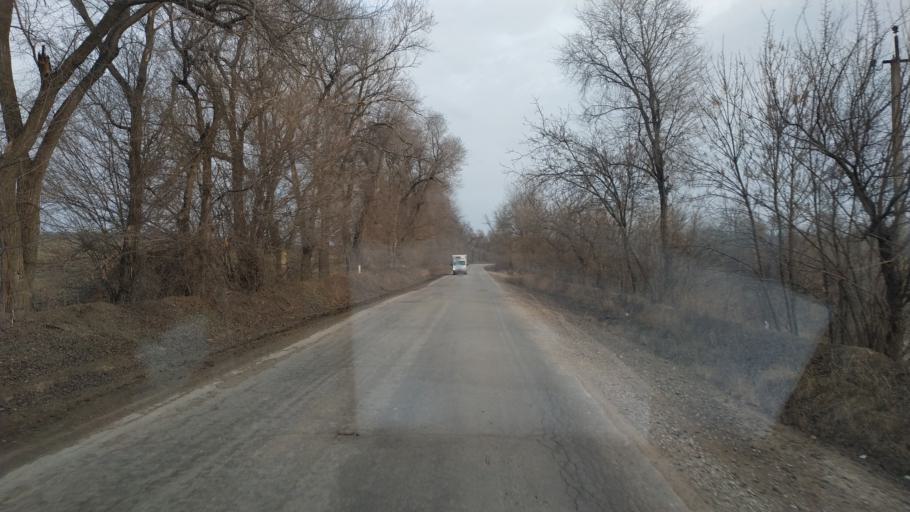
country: MD
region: Chisinau
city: Singera
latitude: 46.9336
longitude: 29.0470
